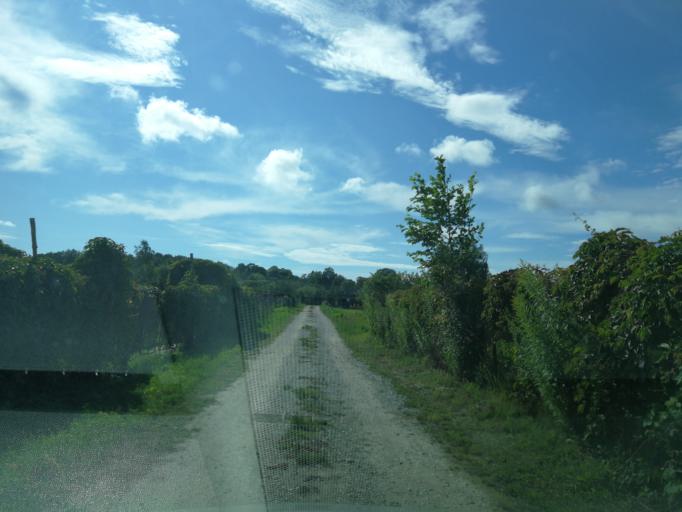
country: LV
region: Adazi
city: Adazi
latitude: 57.0942
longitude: 24.3228
